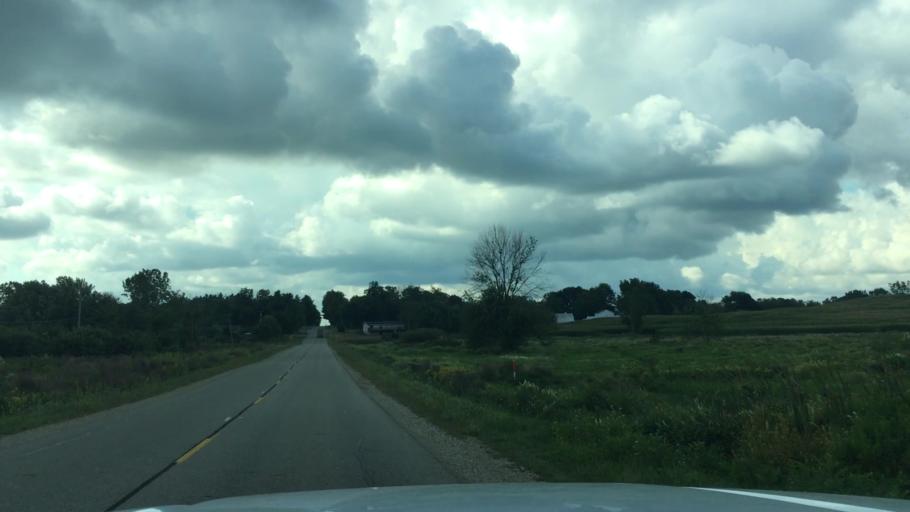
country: US
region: Michigan
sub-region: Ottawa County
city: Hudsonville
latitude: 42.7864
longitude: -85.8417
